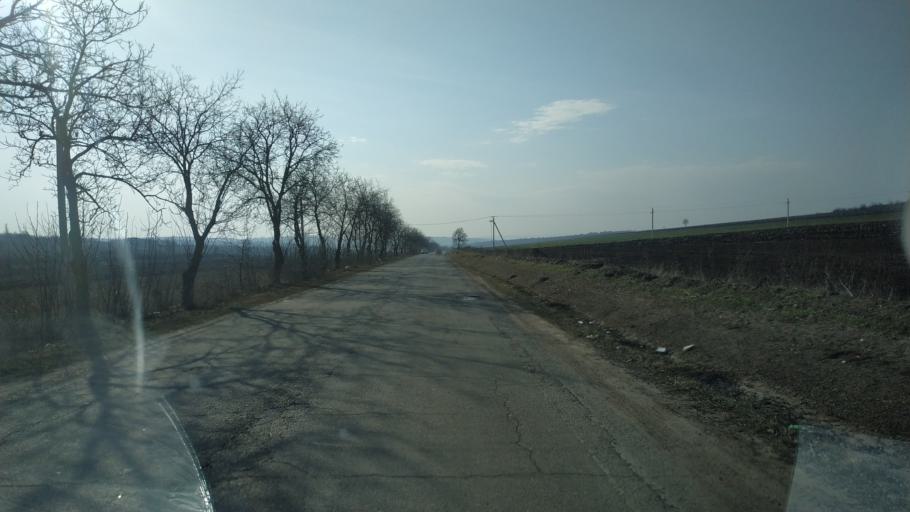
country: MD
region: Chisinau
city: Singera
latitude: 46.8550
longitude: 29.0214
